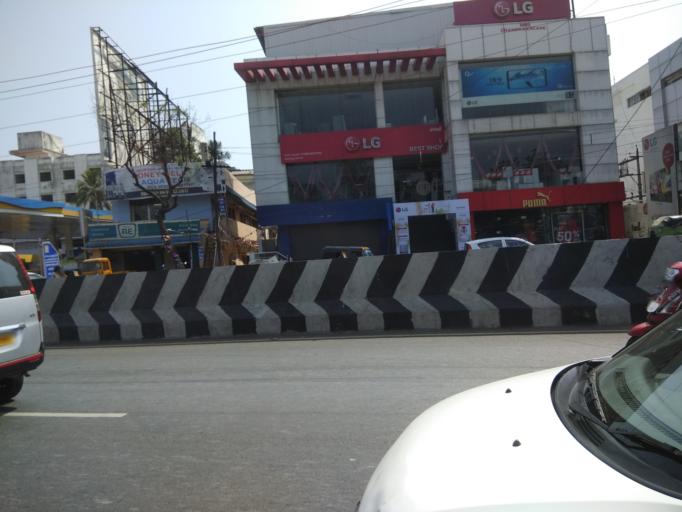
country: IN
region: Tamil Nadu
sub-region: Kancheepuram
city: Pallavaram
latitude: 12.9437
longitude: 80.1342
